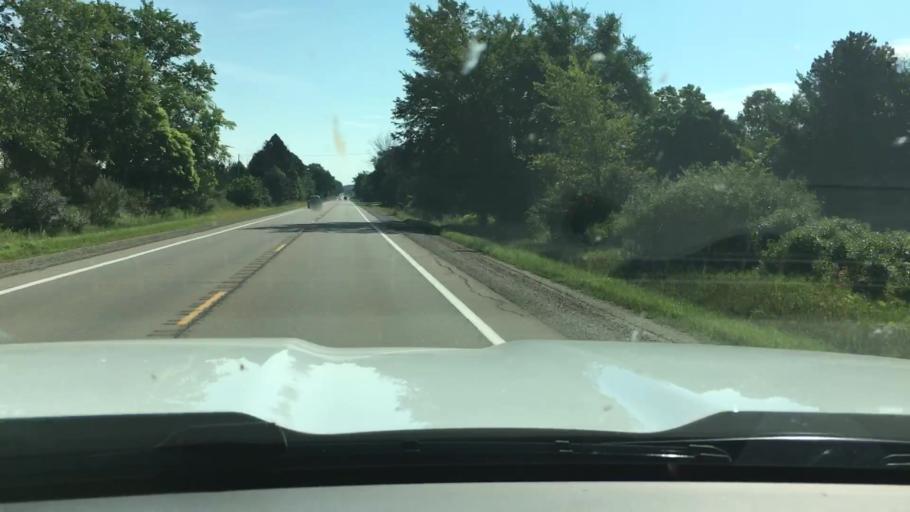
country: US
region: Michigan
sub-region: Gratiot County
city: Alma
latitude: 43.4082
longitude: -84.7591
